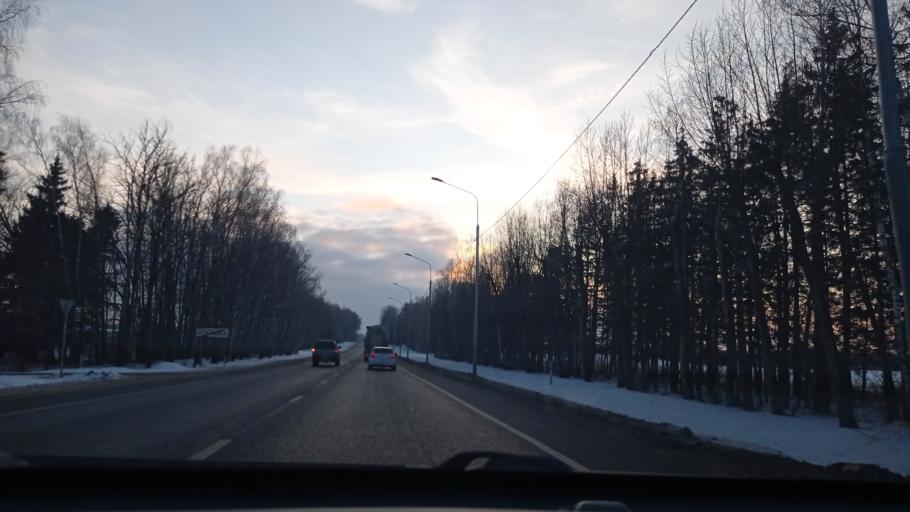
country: RU
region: Moskovskaya
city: Troitsk
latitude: 55.2965
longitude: 37.1342
